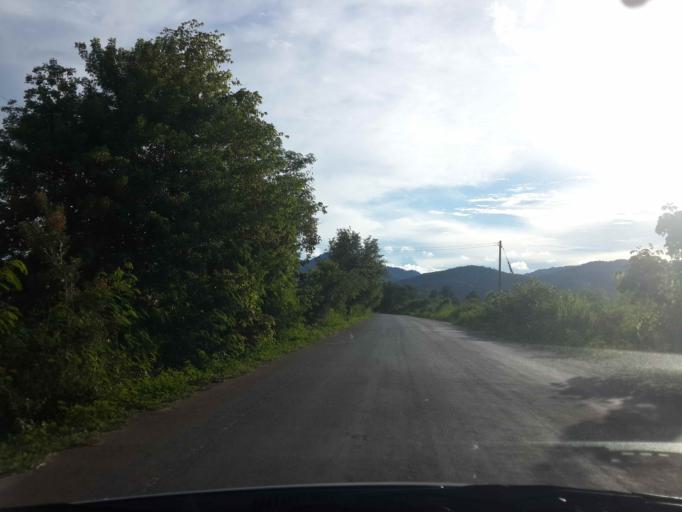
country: TH
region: Kanchanaburi
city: Dan Makham Tia
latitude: 13.8756
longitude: 99.1670
